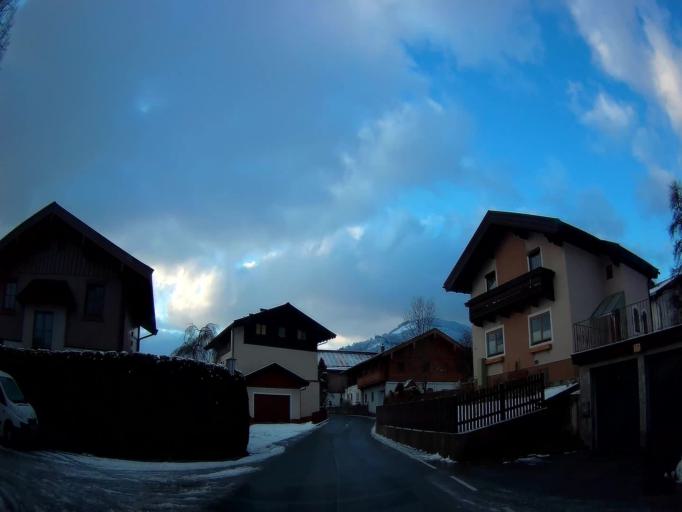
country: AT
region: Salzburg
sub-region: Politischer Bezirk Zell am See
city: Saalfelden am Steinernen Meer
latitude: 47.4506
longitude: 12.8194
